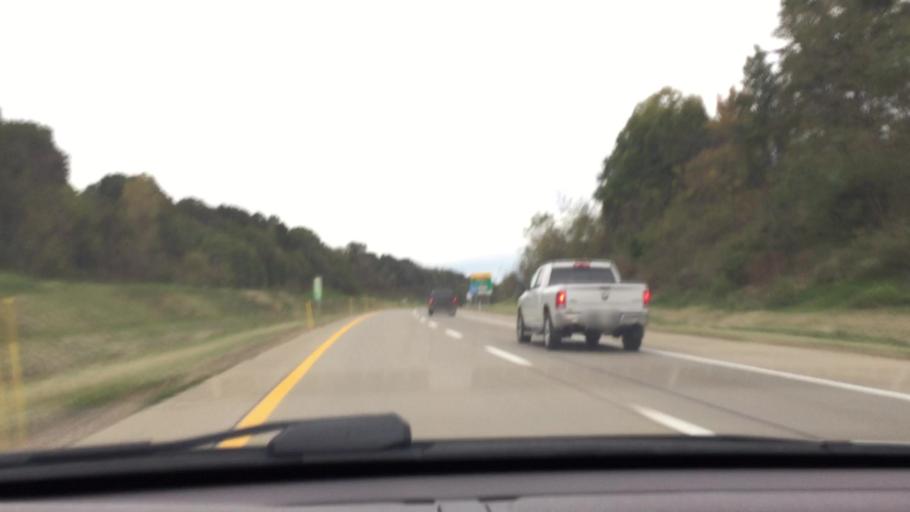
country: US
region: Pennsylvania
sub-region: Lawrence County
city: New Beaver
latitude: 40.9315
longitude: -80.3904
